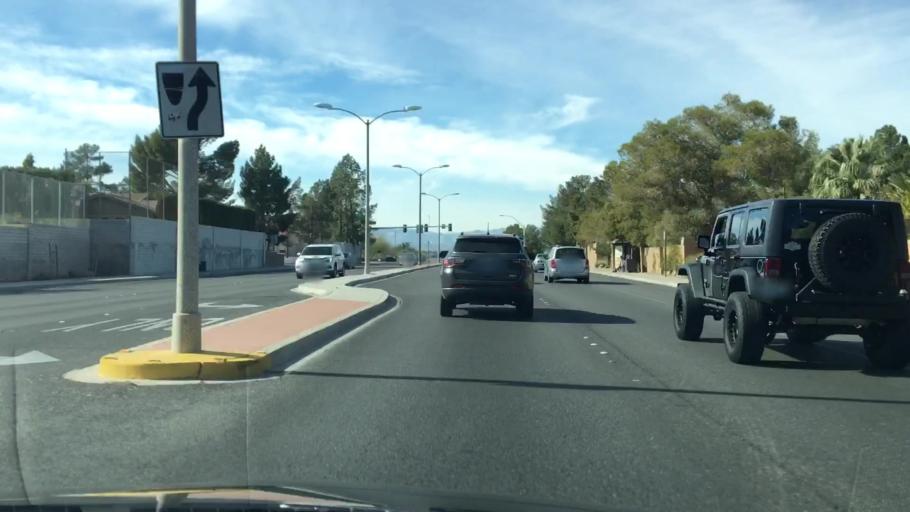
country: US
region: Nevada
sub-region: Clark County
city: Whitney
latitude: 36.0570
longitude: -115.0985
